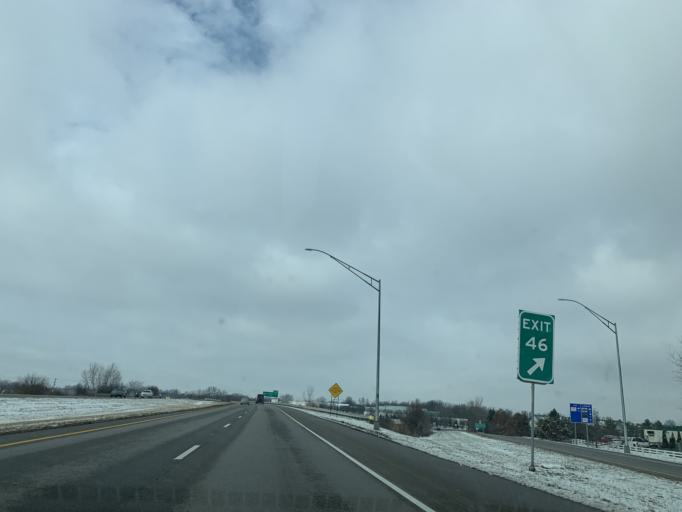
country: US
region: Ohio
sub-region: Franklin County
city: New Albany
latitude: 40.0862
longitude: -82.7959
